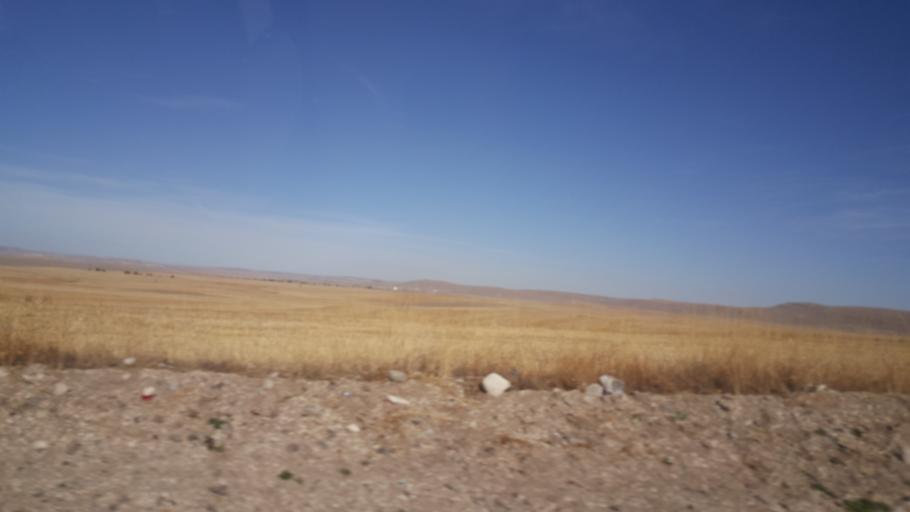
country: TR
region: Ankara
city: Yenice
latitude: 39.3293
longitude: 32.7540
